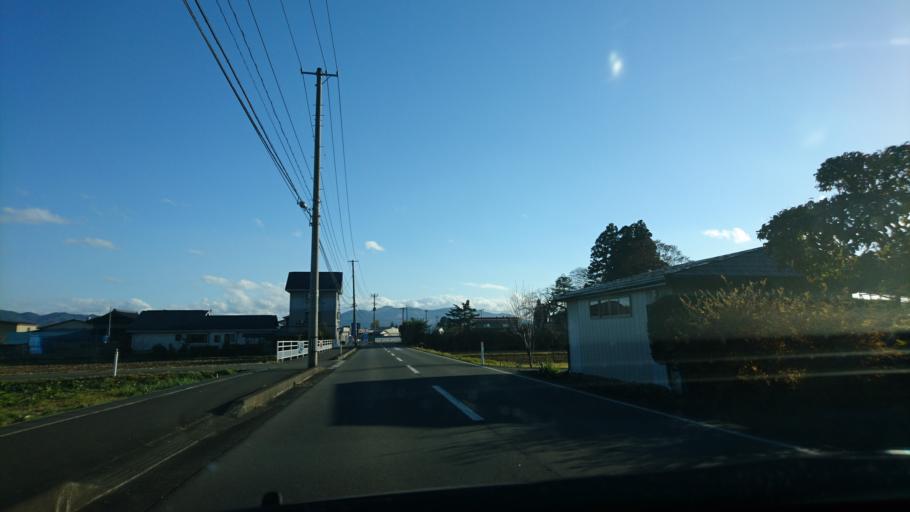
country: JP
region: Iwate
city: Mizusawa
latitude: 39.1101
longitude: 141.1559
